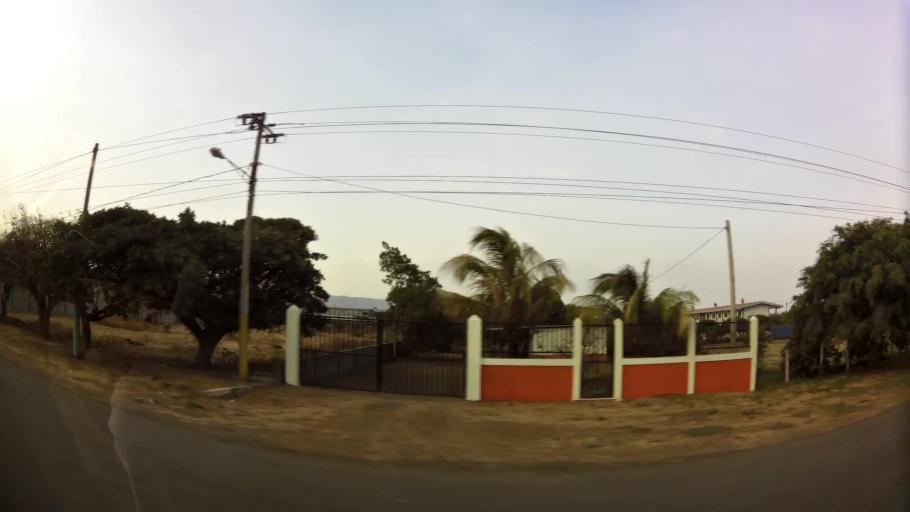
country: NI
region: Managua
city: Ciudad Sandino
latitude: 12.1815
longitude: -86.3568
